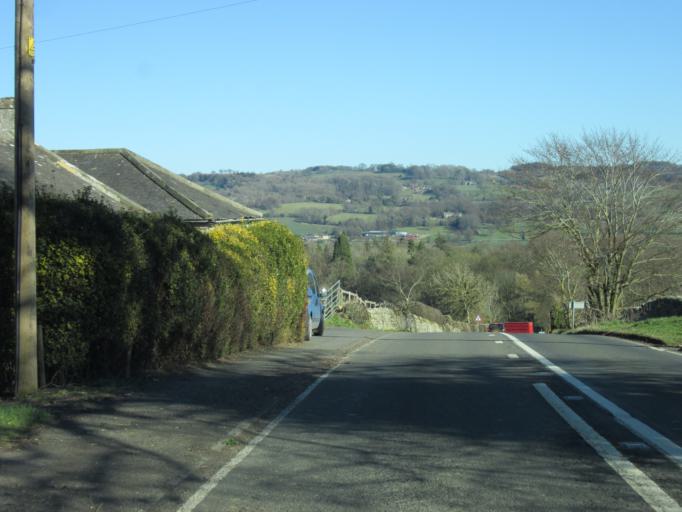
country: GB
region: England
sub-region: Northumberland
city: Wall
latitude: 55.0292
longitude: -2.1523
